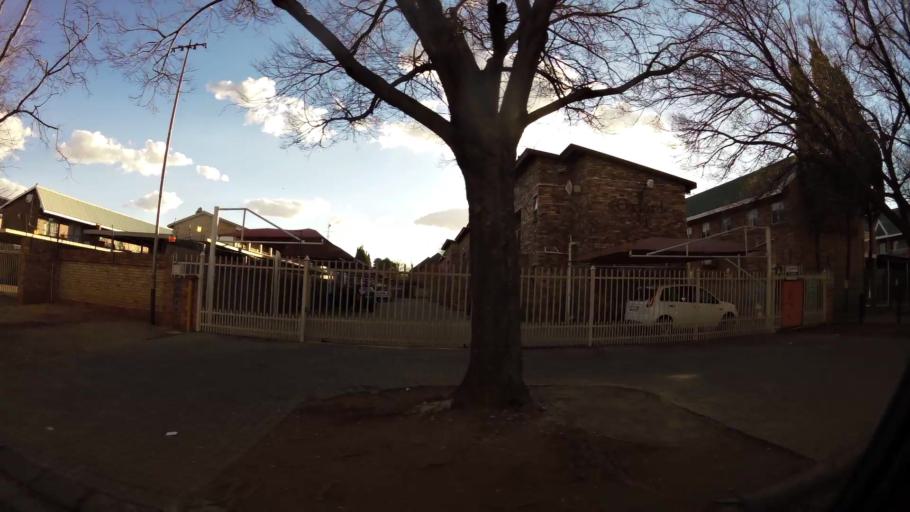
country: ZA
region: North-West
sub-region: Dr Kenneth Kaunda District Municipality
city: Potchefstroom
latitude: -26.6993
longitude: 27.0888
